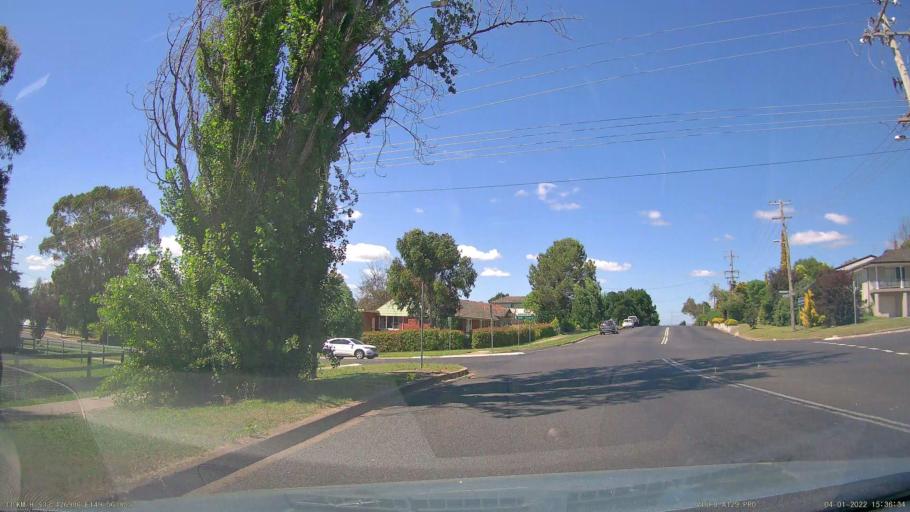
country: AU
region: New South Wales
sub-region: Bathurst Regional
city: Bathurst
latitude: -33.4270
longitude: 149.5679
